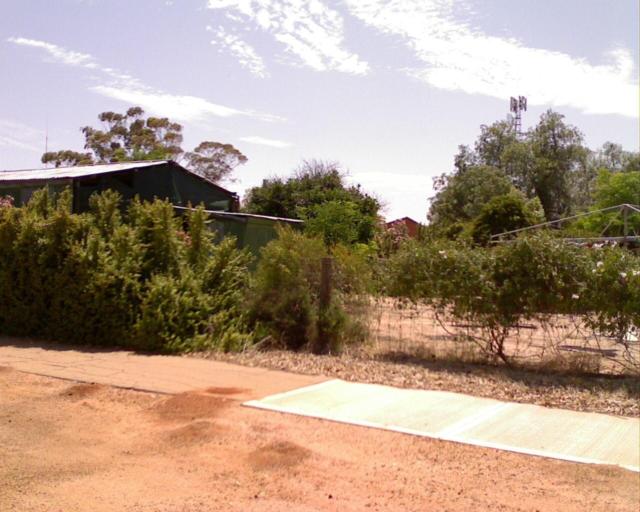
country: AU
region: Western Australia
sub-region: Merredin
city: Merredin
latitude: -30.9154
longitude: 118.2046
